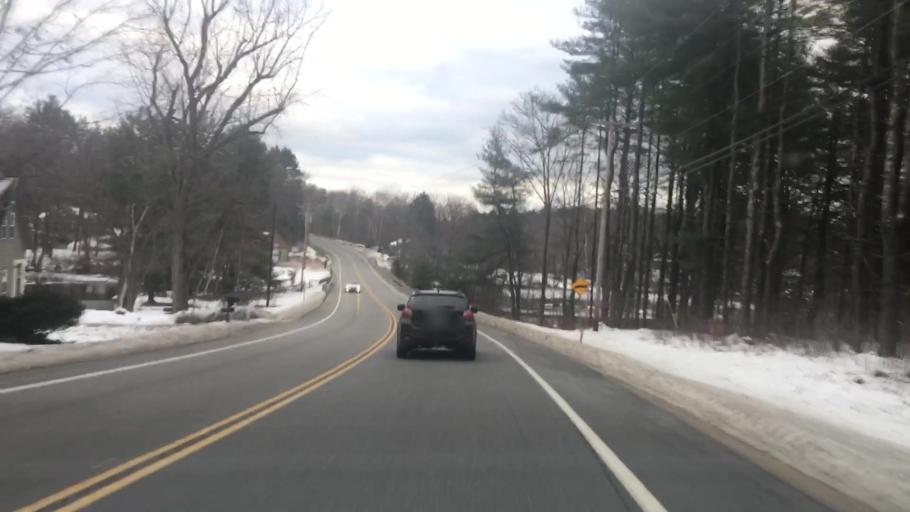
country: US
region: New Hampshire
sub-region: Hillsborough County
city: Antrim
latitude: 43.0815
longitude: -71.9722
